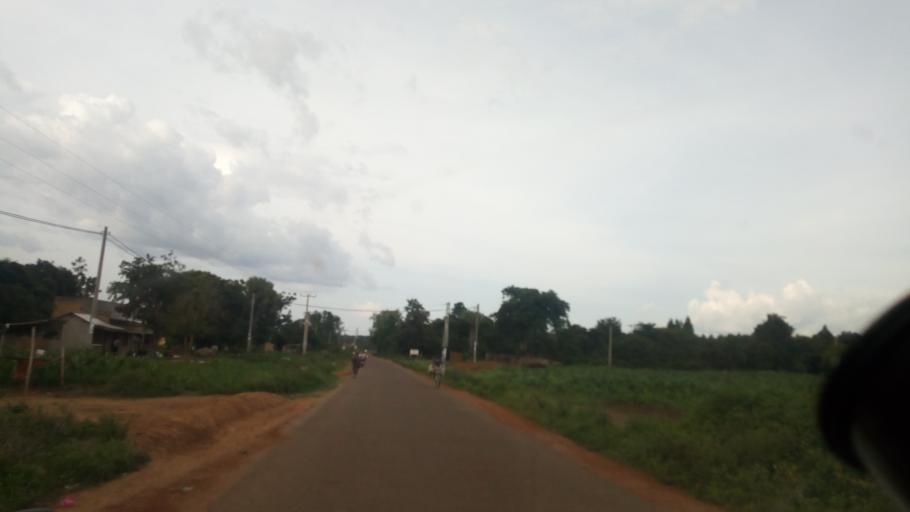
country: UG
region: Northern Region
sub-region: Lira District
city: Lira
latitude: 2.2597
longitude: 32.8563
